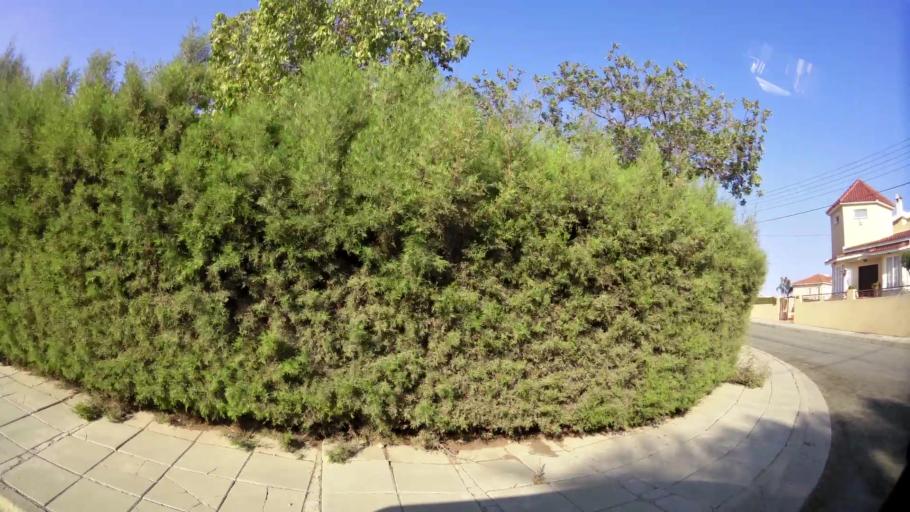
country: CY
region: Larnaka
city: Aradippou
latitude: 34.9416
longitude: 33.6015
